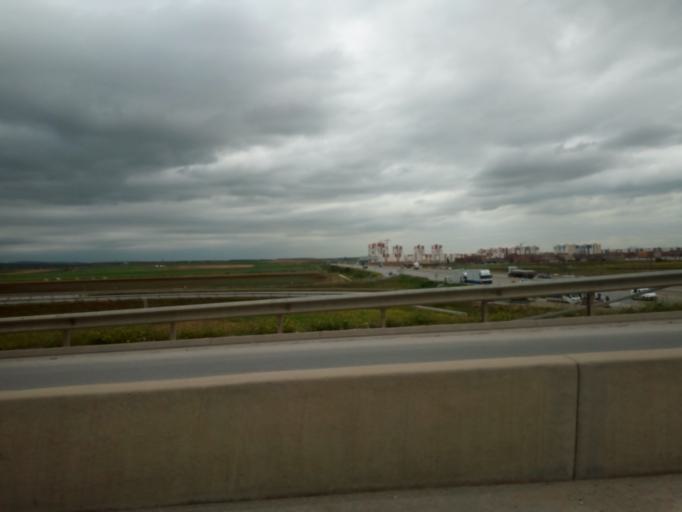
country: DZ
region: Setif
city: El Eulma
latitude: 36.1775
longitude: 5.6746
